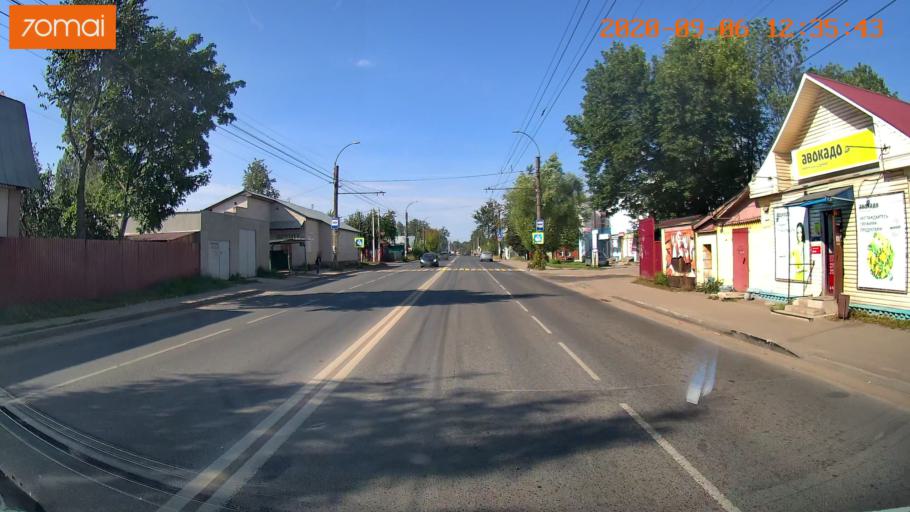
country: RU
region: Ivanovo
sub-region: Gorod Ivanovo
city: Ivanovo
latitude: 57.0206
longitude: 40.9910
